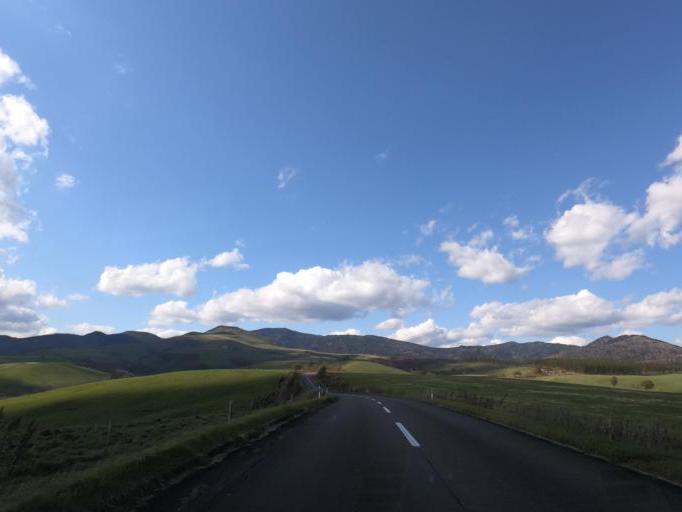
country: JP
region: Hokkaido
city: Otofuke
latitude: 43.2785
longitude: 143.2260
